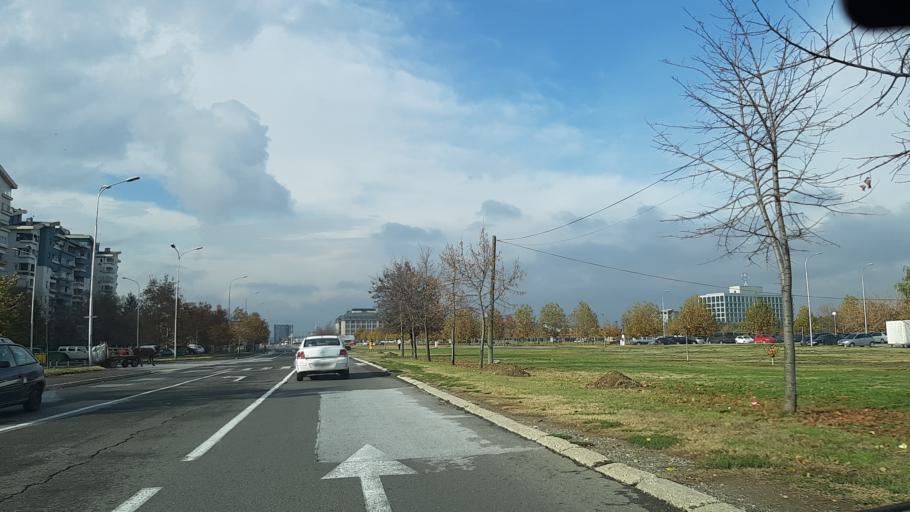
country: MK
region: Kisela Voda
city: Usje
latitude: 41.9877
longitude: 21.4785
